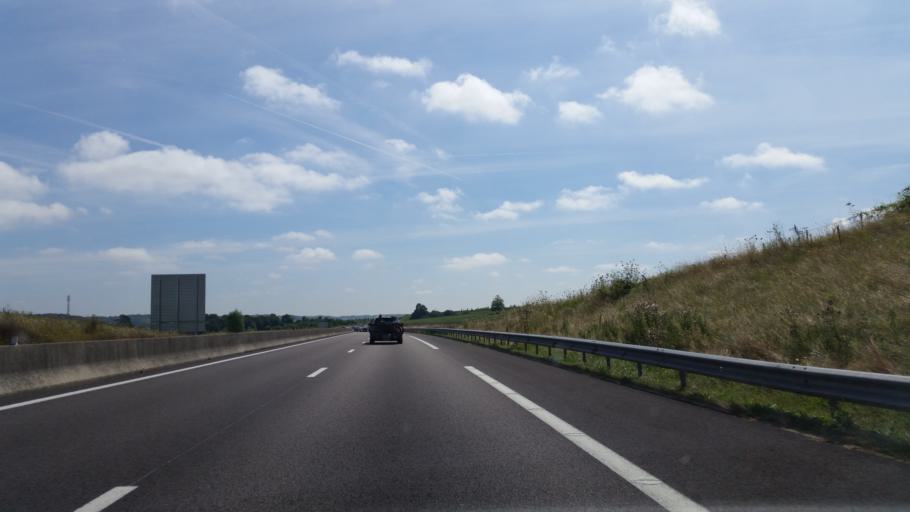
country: FR
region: Haute-Normandie
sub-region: Departement de la Seine-Maritime
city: Neufchatel-en-Bray
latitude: 49.7484
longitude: 1.5155
